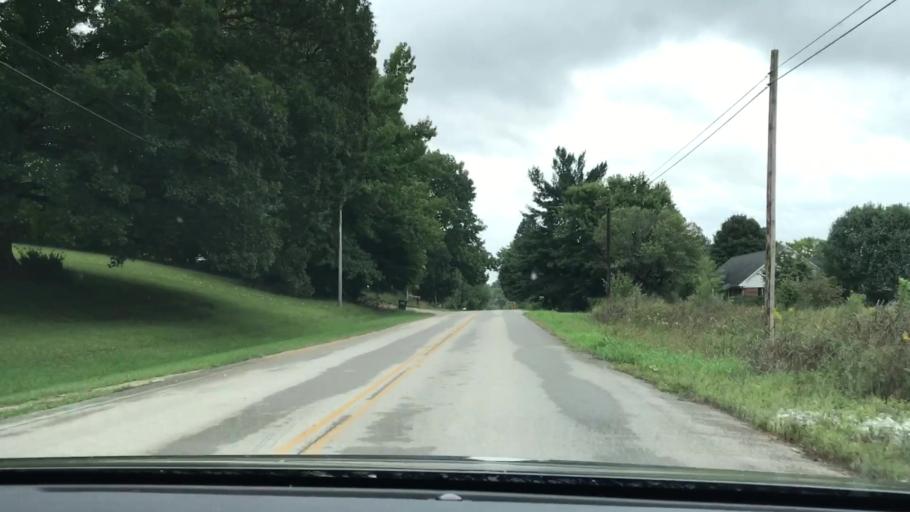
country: US
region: Kentucky
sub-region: Barren County
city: Glasgow
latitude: 36.9687
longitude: -85.8814
